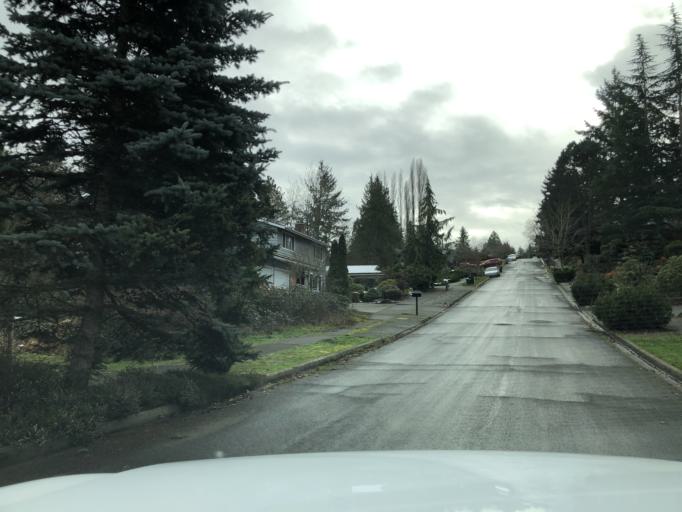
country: US
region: Washington
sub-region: King County
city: Inglewood-Finn Hill
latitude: 47.7001
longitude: -122.2814
